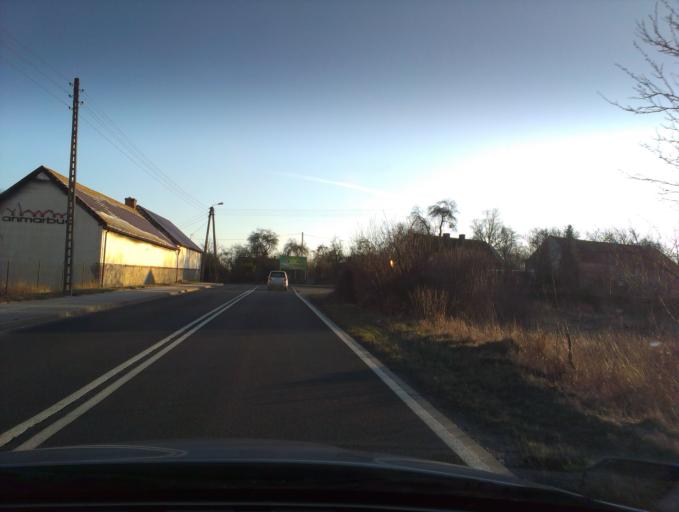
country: PL
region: West Pomeranian Voivodeship
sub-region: Powiat szczecinecki
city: Borne Sulinowo
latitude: 53.6273
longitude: 16.6028
